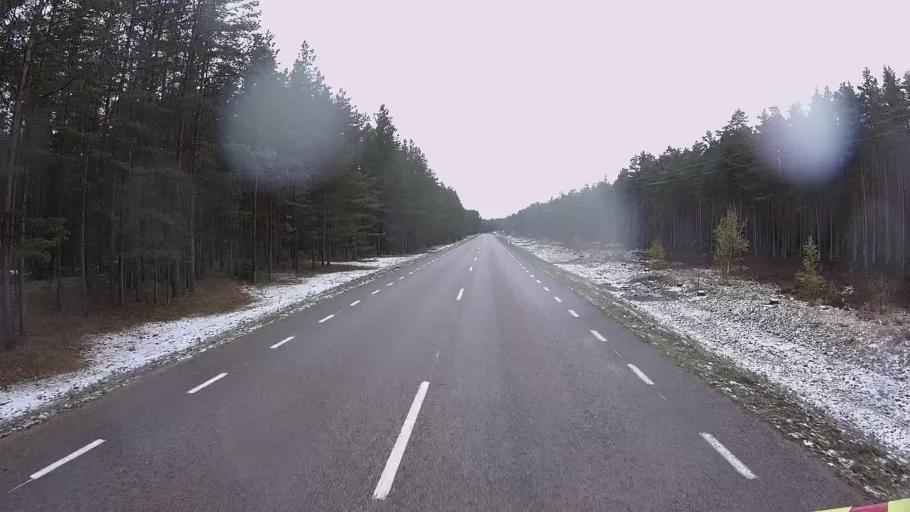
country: EE
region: Hiiumaa
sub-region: Kaerdla linn
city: Kardla
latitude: 58.8834
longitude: 22.4416
